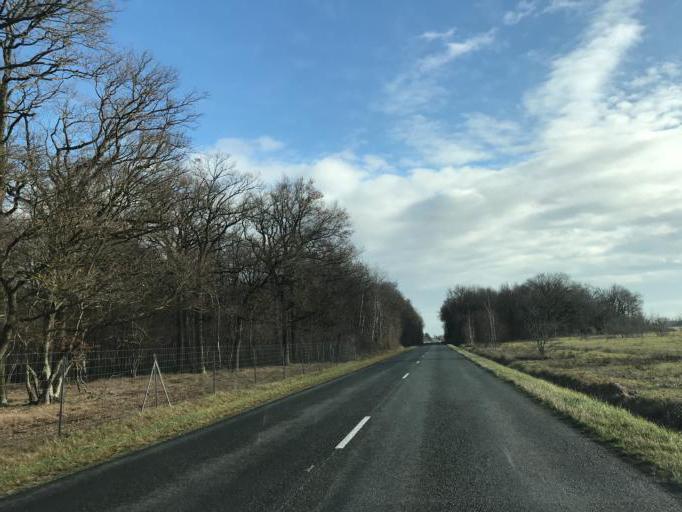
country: FR
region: Rhone-Alpes
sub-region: Departement de l'Ain
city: Saint-Andre-de-Corcy
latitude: 45.9307
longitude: 4.9339
